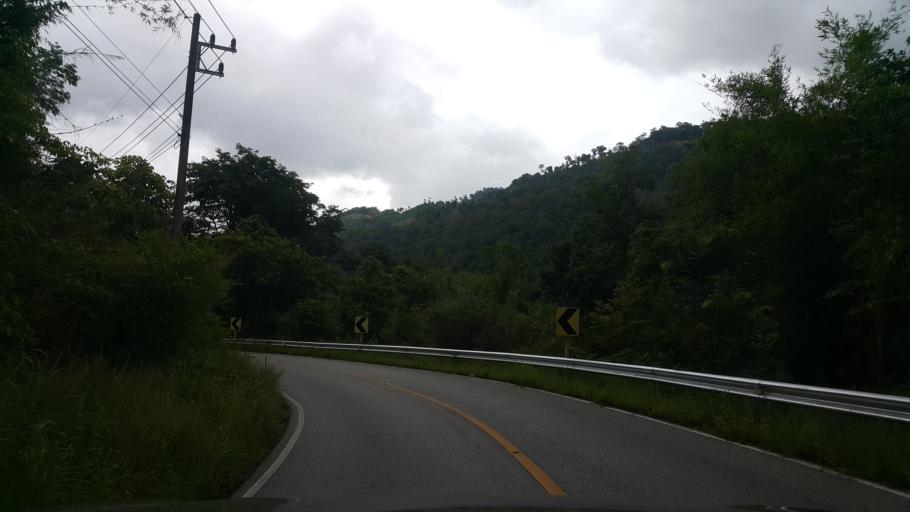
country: TH
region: Loei
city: Na Haeo
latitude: 17.5007
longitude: 100.8171
